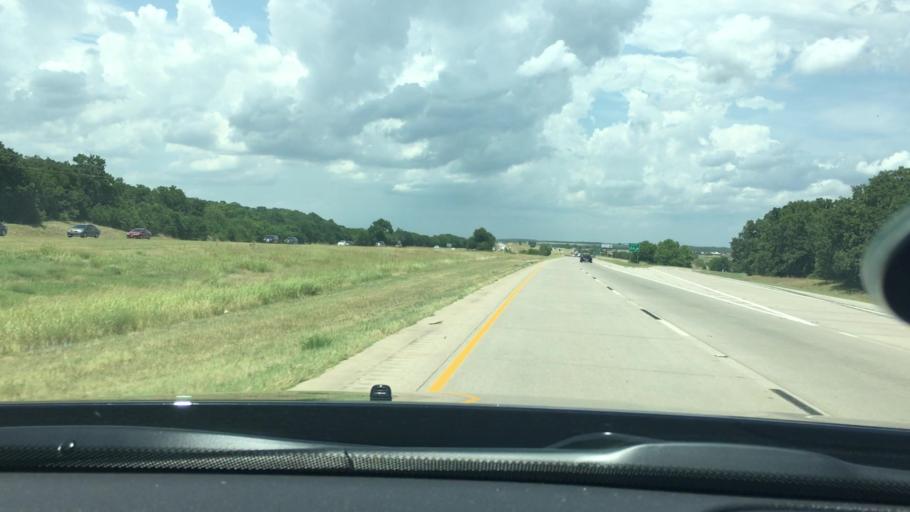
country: US
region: Oklahoma
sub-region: Carter County
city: Ardmore
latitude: 34.0664
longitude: -97.1496
